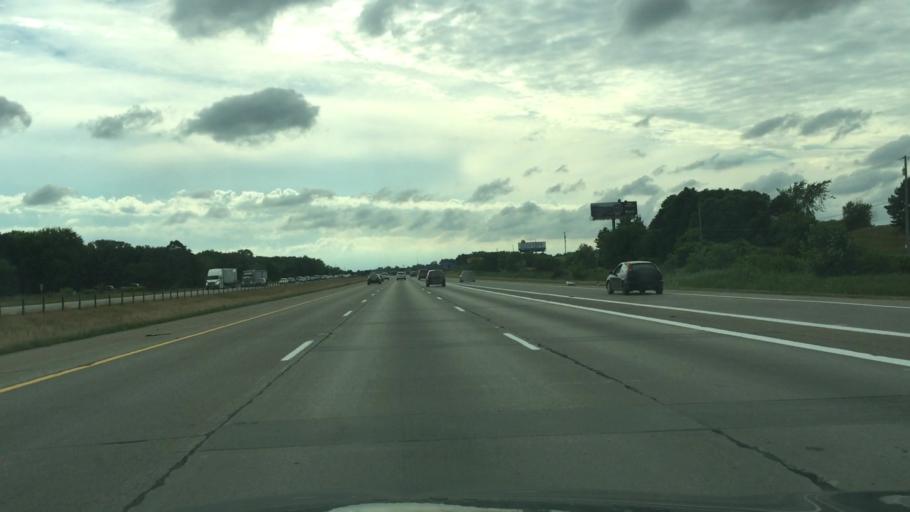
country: US
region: Michigan
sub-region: Wayne County
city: Belleville
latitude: 42.2191
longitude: -83.5237
